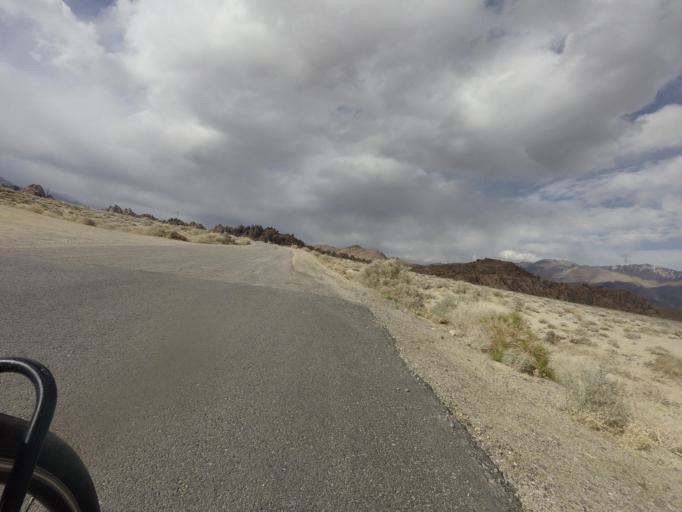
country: US
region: California
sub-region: Inyo County
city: Lone Pine
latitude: 36.5957
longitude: -118.1087
